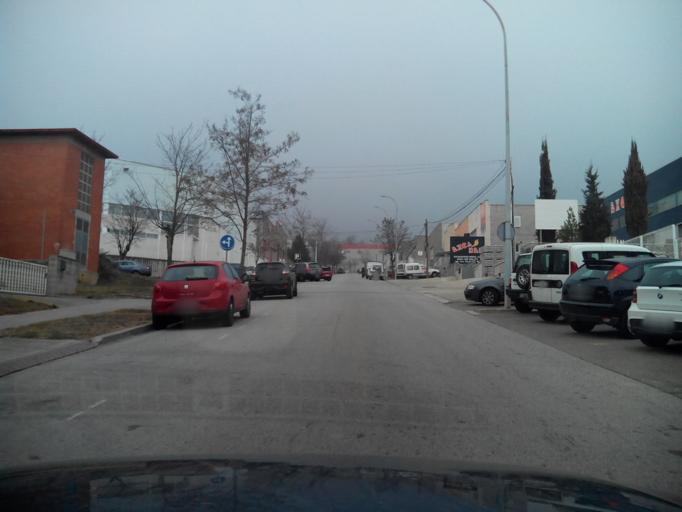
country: ES
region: Catalonia
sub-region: Provincia de Barcelona
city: Berga
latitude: 42.0951
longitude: 1.8241
